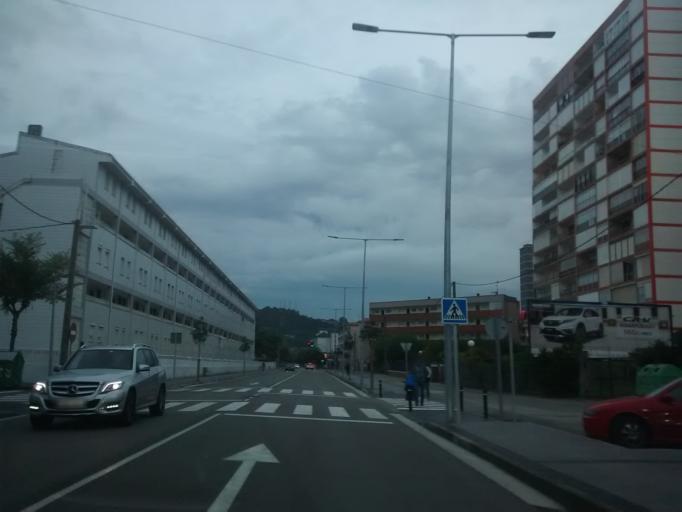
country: ES
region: Cantabria
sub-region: Provincia de Cantabria
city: Laredo
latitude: 43.4117
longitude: -3.4373
